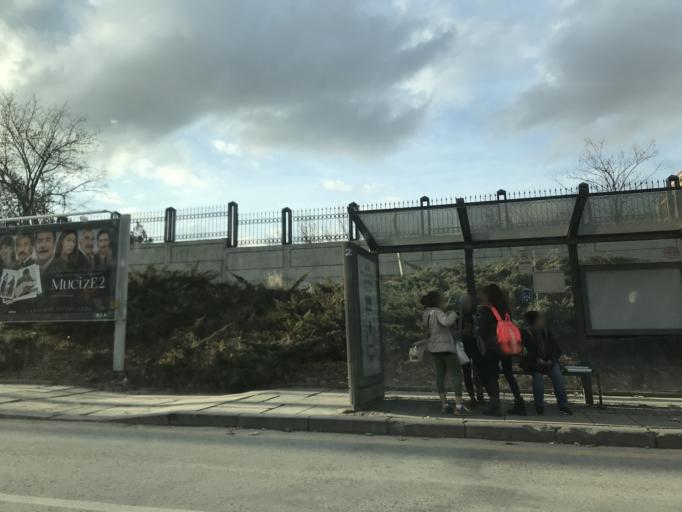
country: TR
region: Ankara
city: Cankaya
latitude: 39.9626
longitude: 32.8688
